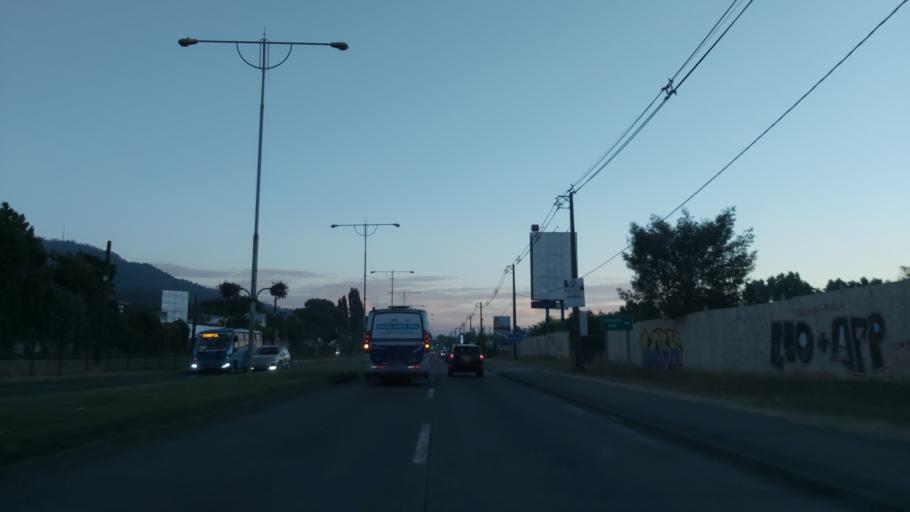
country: CL
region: Biobio
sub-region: Provincia de Concepcion
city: Chiguayante
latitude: -36.8971
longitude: -73.0330
